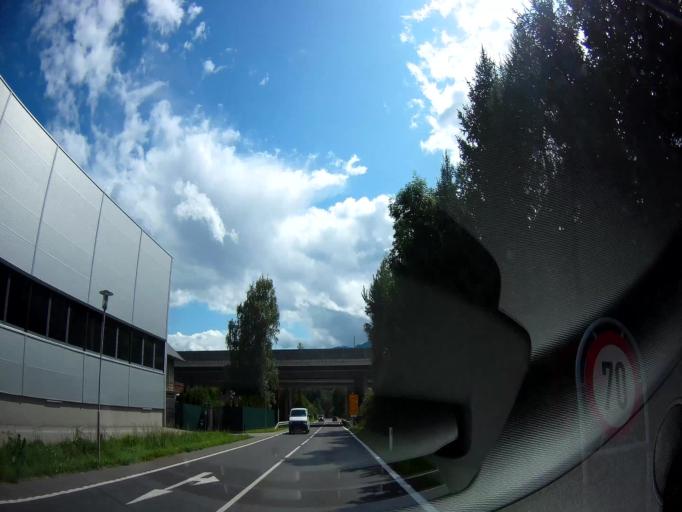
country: AT
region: Carinthia
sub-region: Politischer Bezirk Spittal an der Drau
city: Seeboden
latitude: 46.8263
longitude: 13.4907
